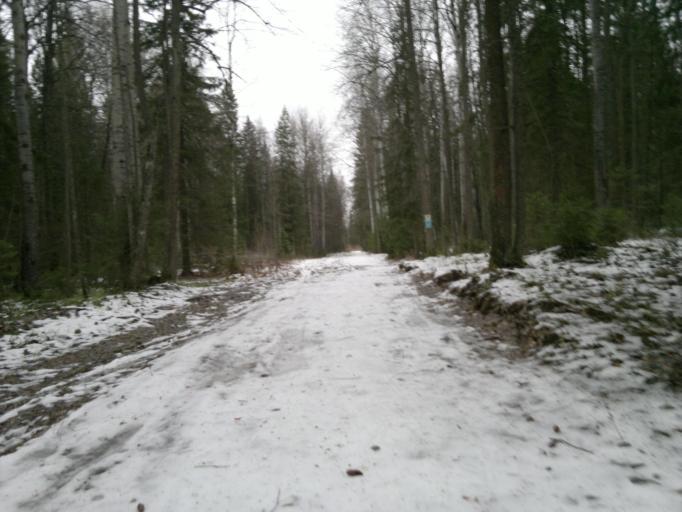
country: RU
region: Mariy-El
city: Yoshkar-Ola
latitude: 56.5922
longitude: 47.9675
